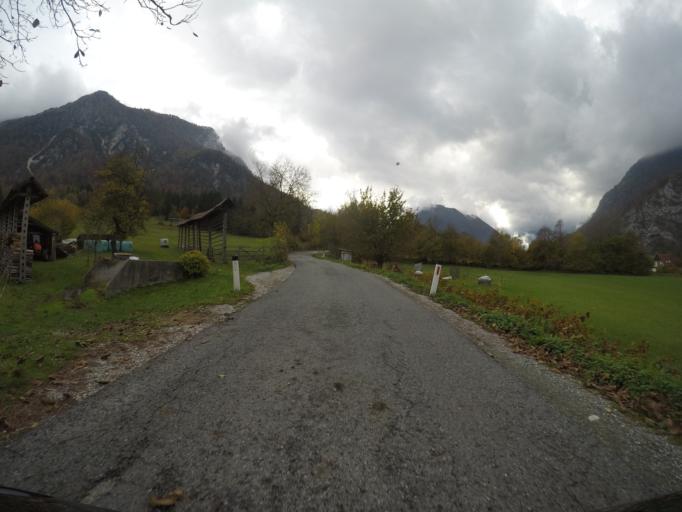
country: SI
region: Kranjska Gora
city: Mojstrana
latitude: 46.4598
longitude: 13.9421
